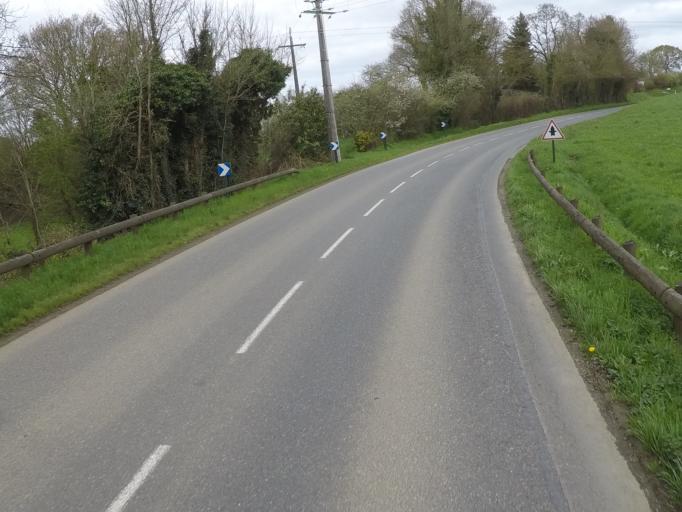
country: FR
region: Brittany
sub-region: Departement des Cotes-d'Armor
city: Pleguien
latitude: 48.6494
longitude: -2.9640
